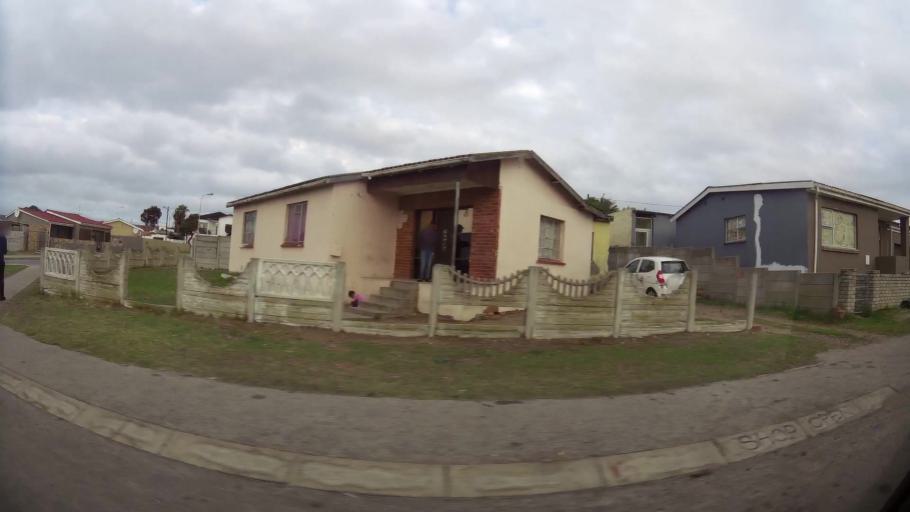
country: ZA
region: Eastern Cape
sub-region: Nelson Mandela Bay Metropolitan Municipality
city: Port Elizabeth
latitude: -33.9129
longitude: 25.5541
